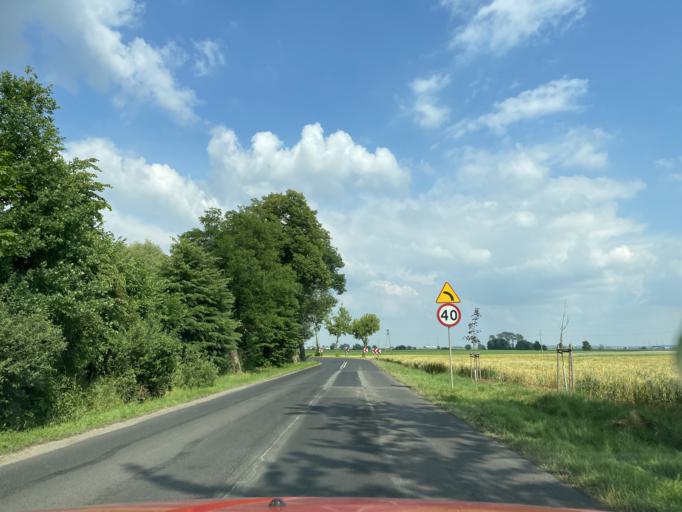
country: PL
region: Greater Poland Voivodeship
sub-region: Powiat poznanski
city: Dopiewo
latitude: 52.3586
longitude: 16.7148
